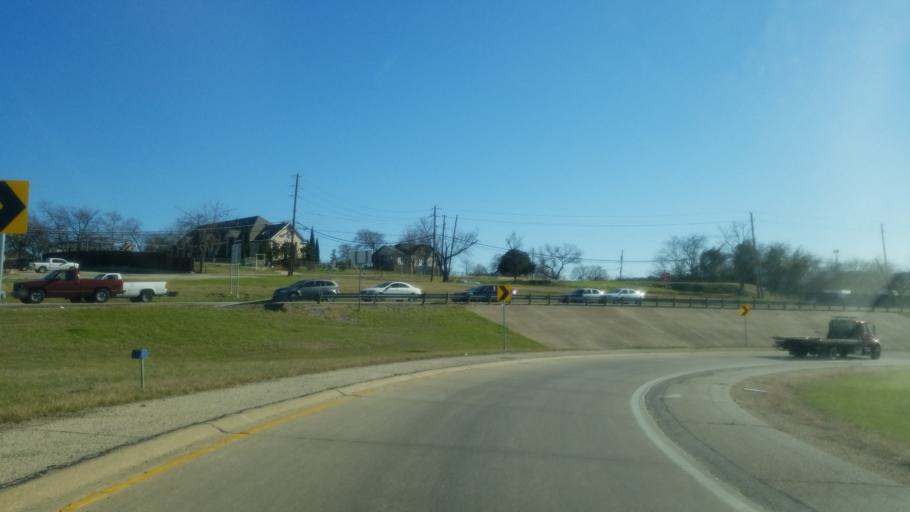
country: US
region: Texas
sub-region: Dallas County
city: Cockrell Hill
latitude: 32.7474
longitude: -96.9175
